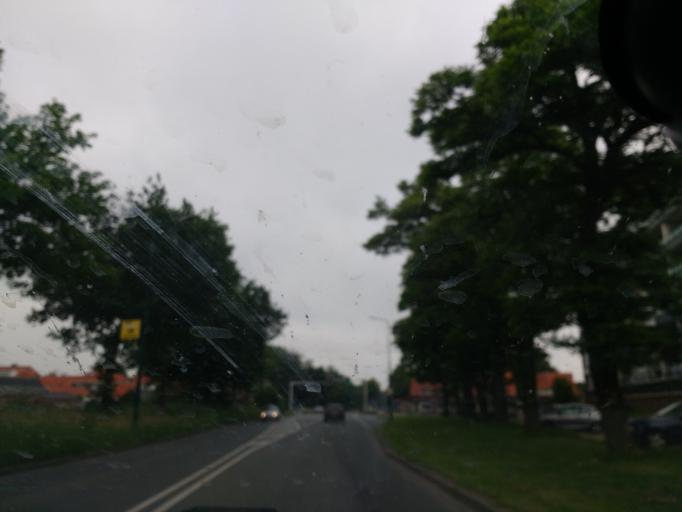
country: NL
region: Utrecht
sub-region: Gemeente Veenendaal
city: Veenendaal
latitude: 52.0181
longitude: 5.5372
